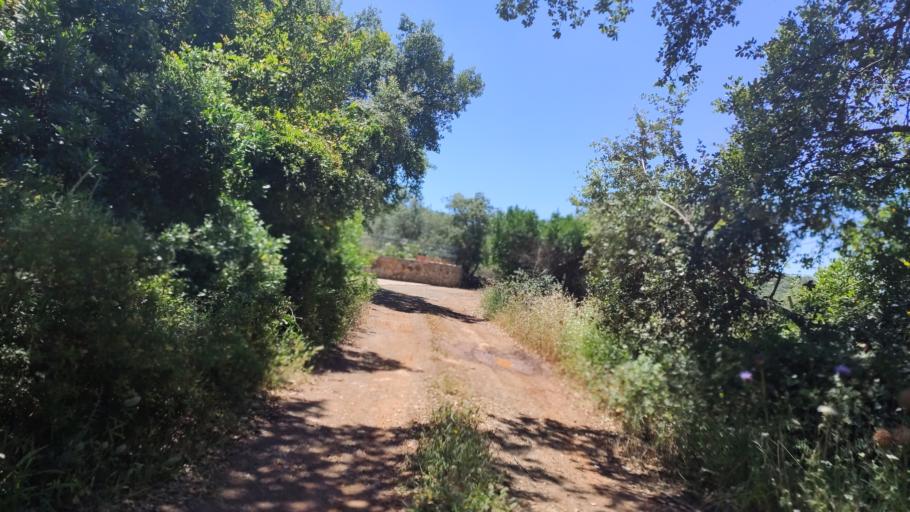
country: PT
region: Faro
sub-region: Sao Bras de Alportel
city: Sao Bras de Alportel
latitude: 37.1633
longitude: -7.9315
